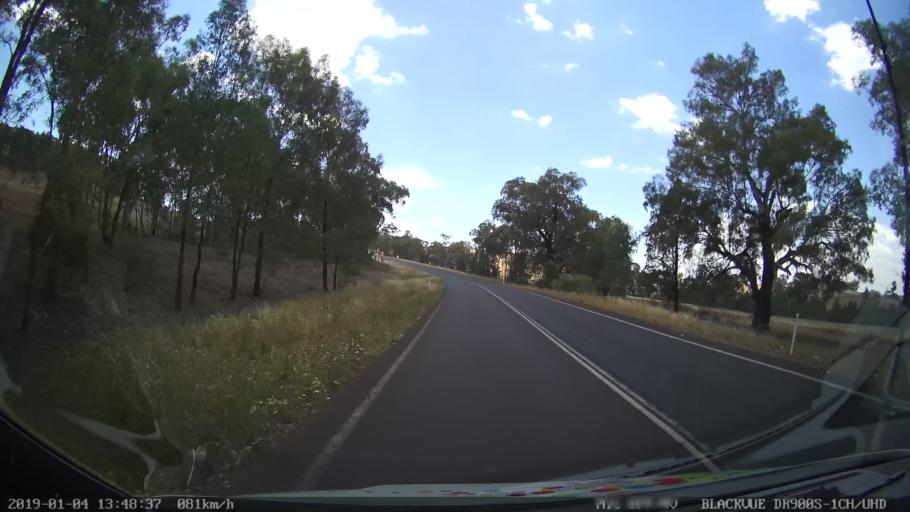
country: AU
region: New South Wales
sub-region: Dubbo Municipality
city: Dubbo
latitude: -32.4405
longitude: 148.5845
